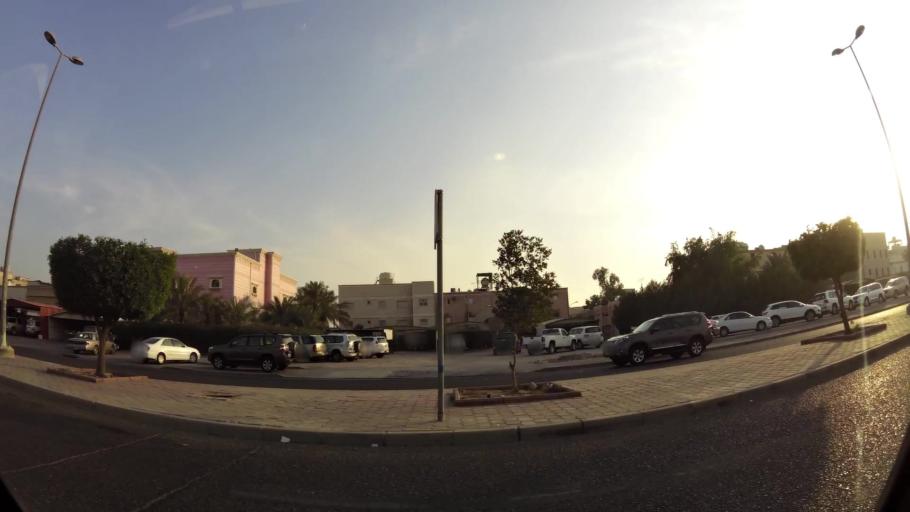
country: KW
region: Mubarak al Kabir
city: Sabah as Salim
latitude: 29.2498
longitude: 48.0726
